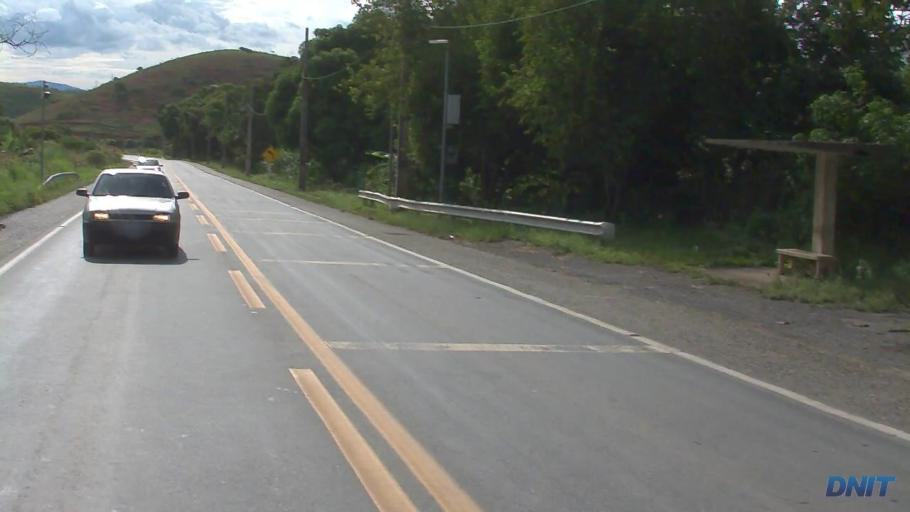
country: BR
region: Minas Gerais
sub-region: Belo Oriente
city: Belo Oriente
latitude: -19.2249
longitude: -42.3244
